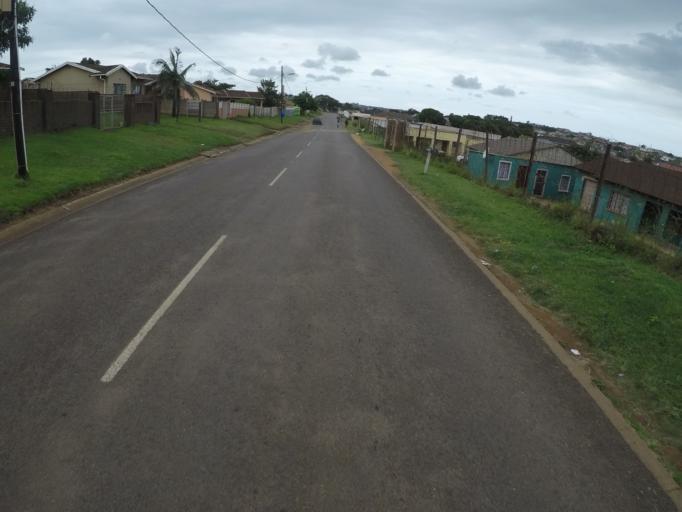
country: ZA
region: KwaZulu-Natal
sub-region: uThungulu District Municipality
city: Empangeni
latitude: -28.7777
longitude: 31.8485
